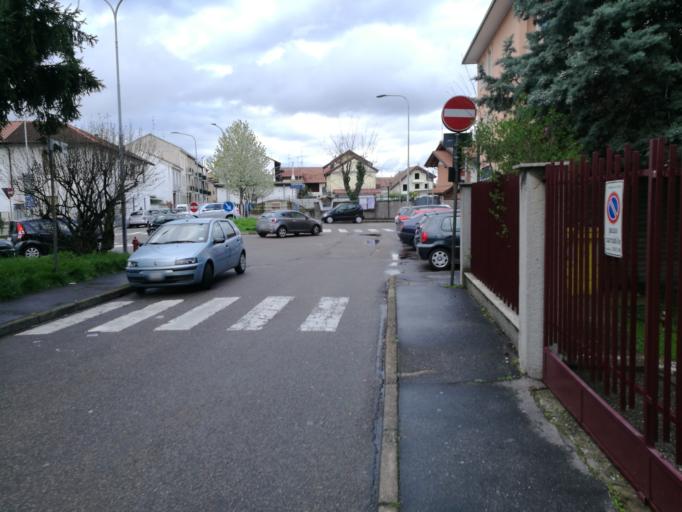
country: IT
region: Lombardy
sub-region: Citta metropolitana di Milano
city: Rho
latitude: 45.5315
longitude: 9.0489
